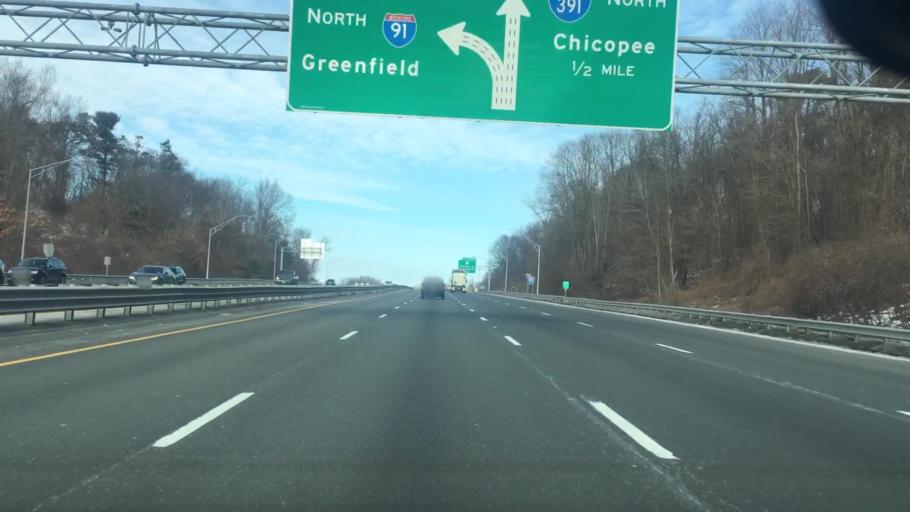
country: US
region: Massachusetts
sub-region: Hampden County
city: Chicopee
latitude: 42.1263
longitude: -72.6081
